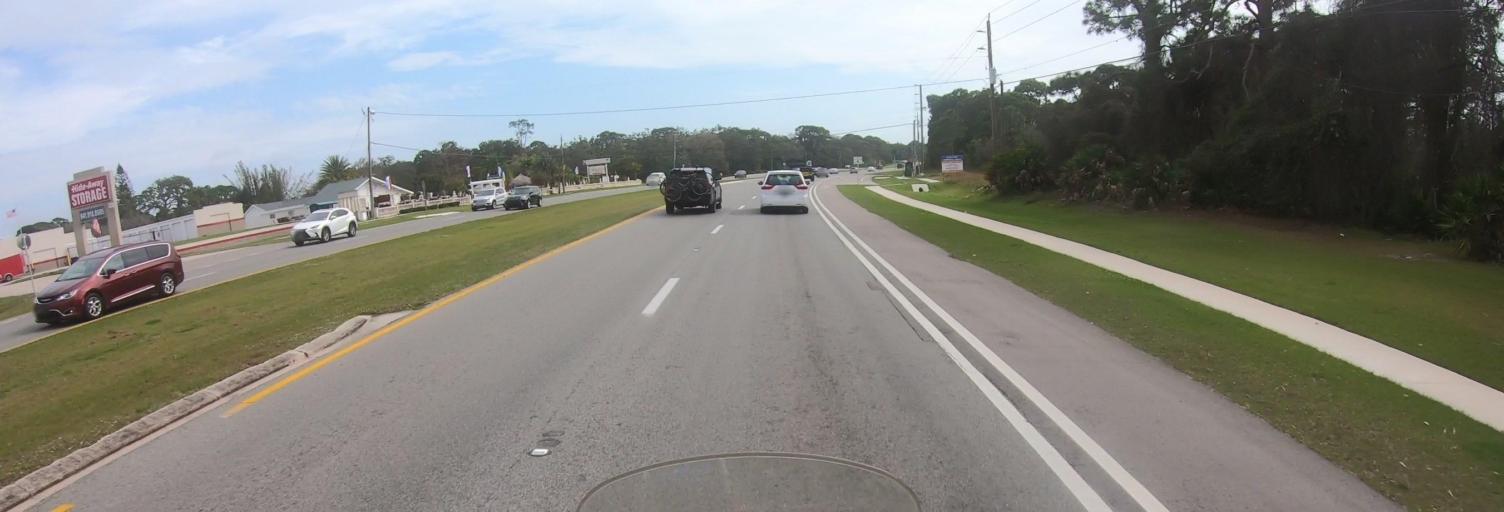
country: US
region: Florida
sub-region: Sarasota County
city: Vamo
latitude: 27.2205
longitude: -82.4918
